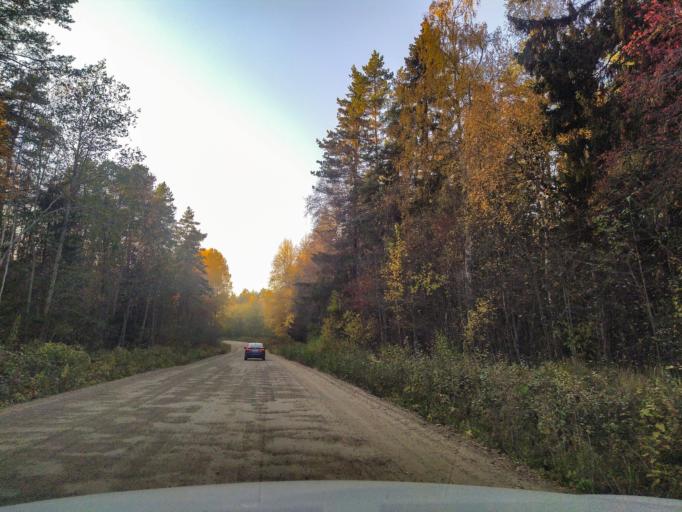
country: RU
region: Leningrad
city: Kuznechnoye
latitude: 61.3302
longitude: 29.9764
